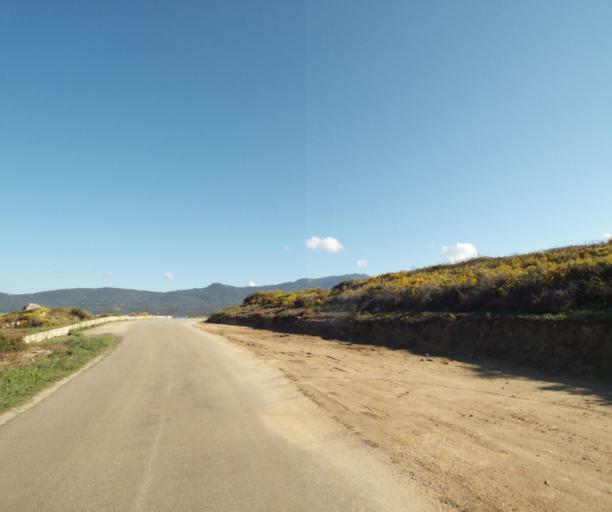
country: FR
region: Corsica
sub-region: Departement de la Corse-du-Sud
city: Propriano
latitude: 41.6654
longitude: 8.8825
